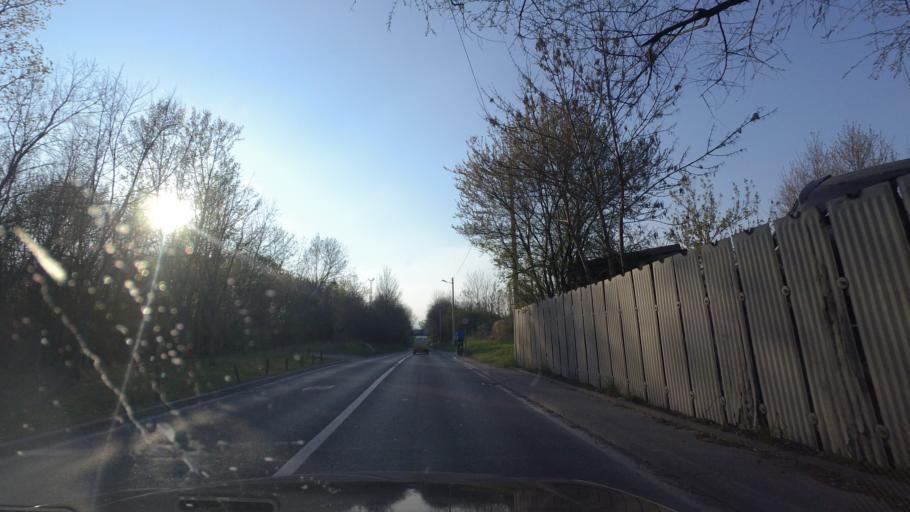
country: HR
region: Grad Zagreb
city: Dubrava
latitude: 45.8071
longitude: 16.0686
